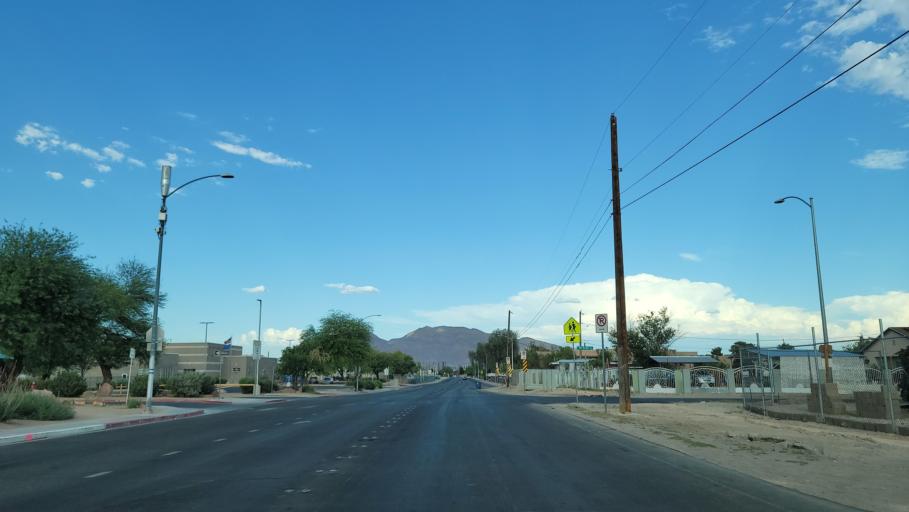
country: US
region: Nevada
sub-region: Clark County
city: North Las Vegas
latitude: 36.1775
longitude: -115.1126
